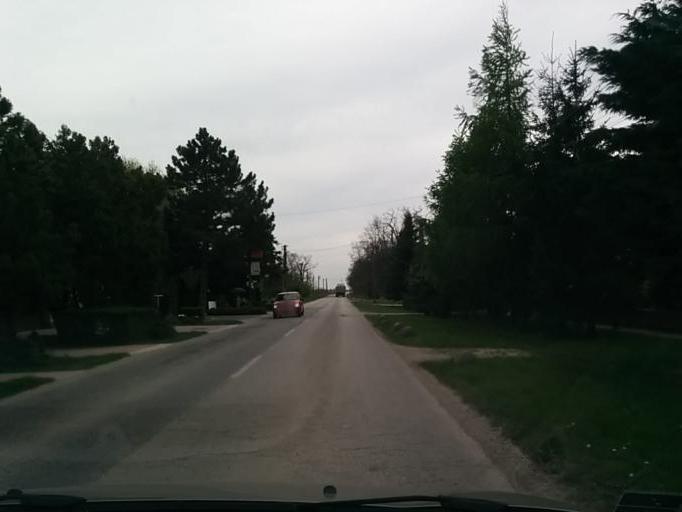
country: SK
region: Bratislavsky
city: Senec
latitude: 48.2453
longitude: 17.4916
